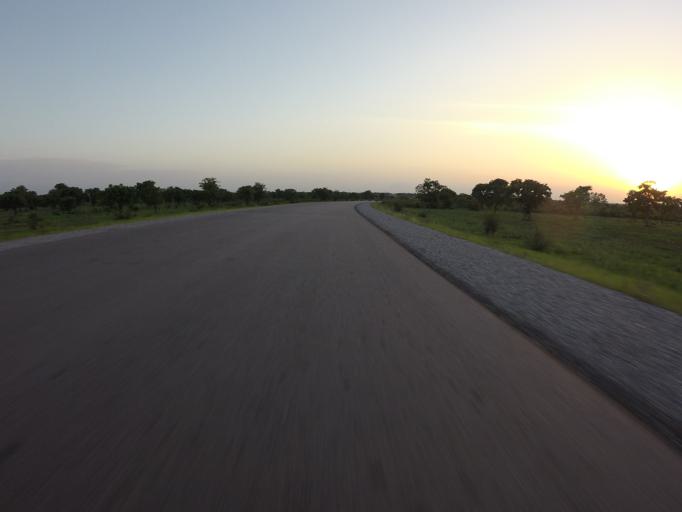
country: GH
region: Northern
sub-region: Yendi
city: Yendi
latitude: 9.9392
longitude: -0.1703
